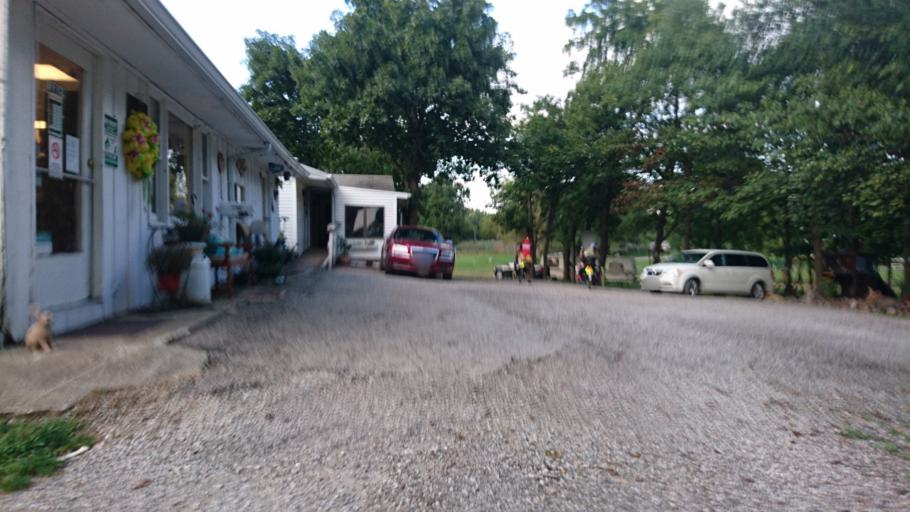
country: US
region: Illinois
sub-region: Logan County
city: Atlanta
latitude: 40.2259
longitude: -89.1975
